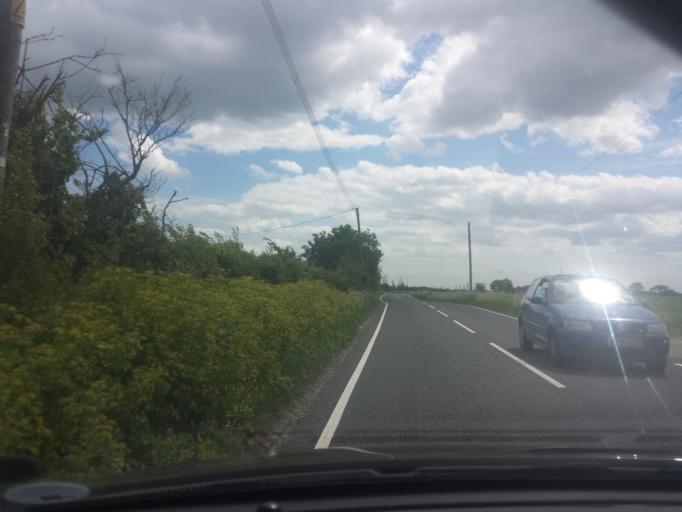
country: GB
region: England
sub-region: Essex
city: Little Clacton
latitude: 51.8381
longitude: 1.1548
